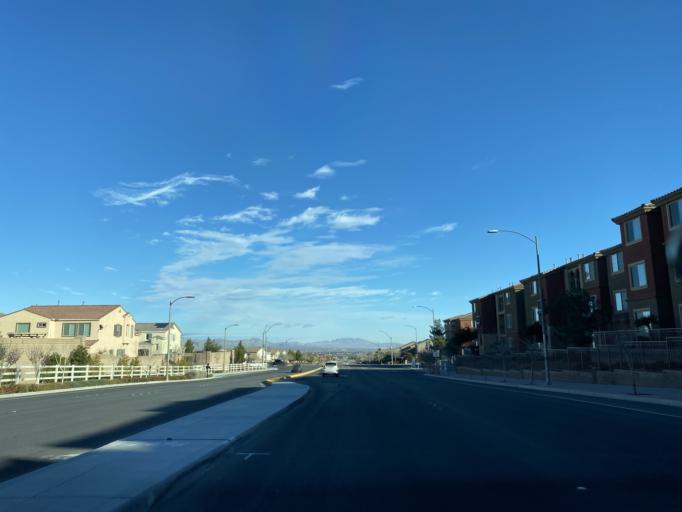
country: US
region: Nevada
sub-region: Clark County
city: Summerlin South
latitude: 36.3067
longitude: -115.3077
